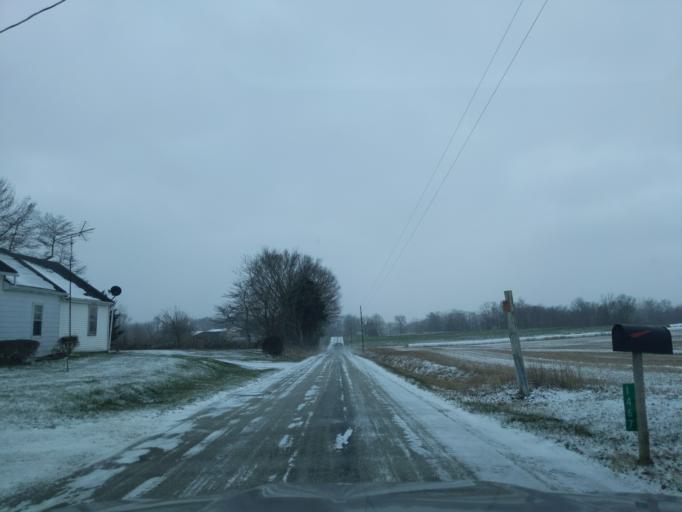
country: US
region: Indiana
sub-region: Decatur County
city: Westport
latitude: 39.2286
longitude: -85.5074
